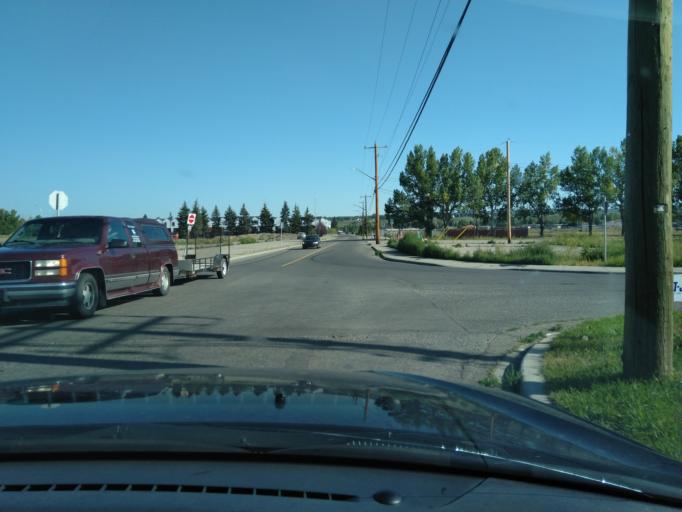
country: CA
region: Alberta
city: Calgary
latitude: 51.0814
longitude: -114.1876
